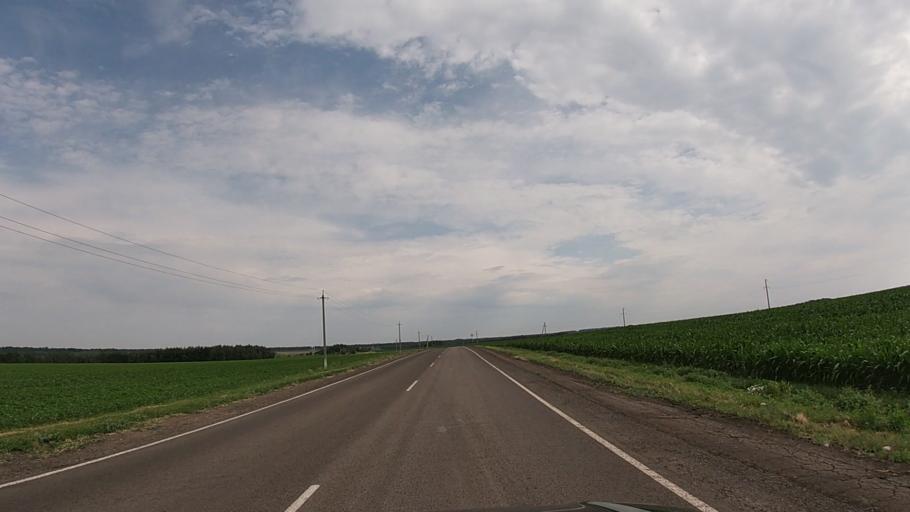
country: RU
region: Belgorod
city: Krasnaya Yaruga
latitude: 50.8170
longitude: 35.5020
